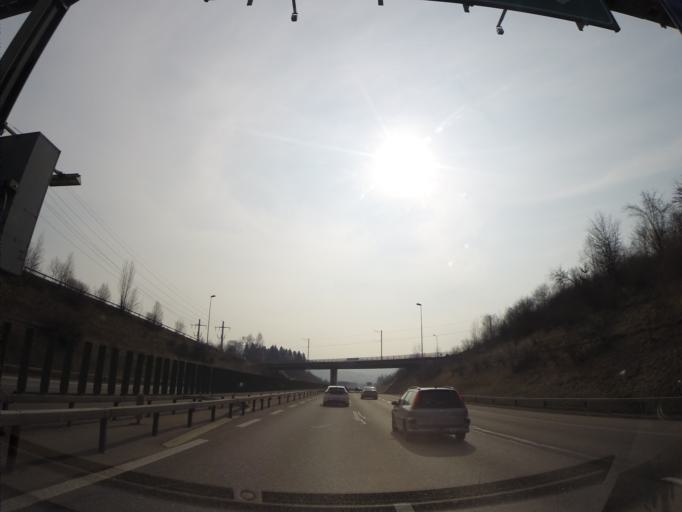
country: CH
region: Zurich
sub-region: Bezirk Winterthur
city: Wuelflingen (Kreis 6) / Lindenplatz
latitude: 47.5192
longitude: 8.6964
